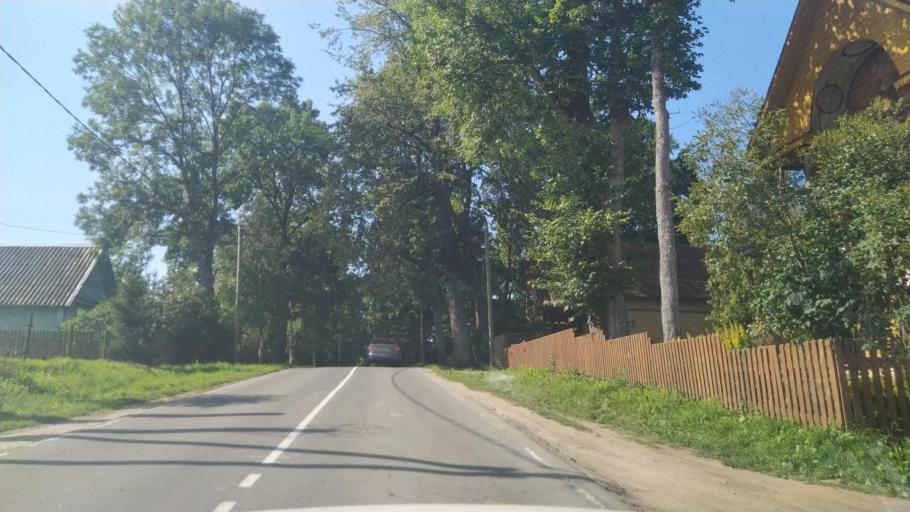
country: RU
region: Leningrad
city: Siverskiy
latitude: 59.2917
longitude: 30.0659
